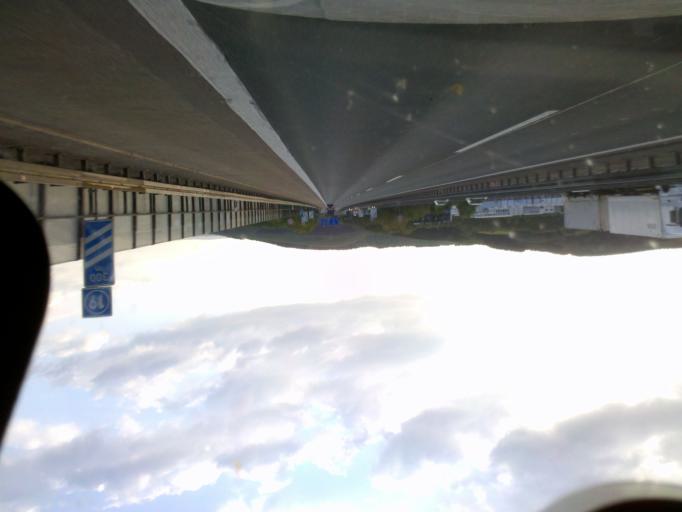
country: DE
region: North Rhine-Westphalia
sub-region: Regierungsbezirk Arnsberg
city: Wenden
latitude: 50.9801
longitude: 7.8408
